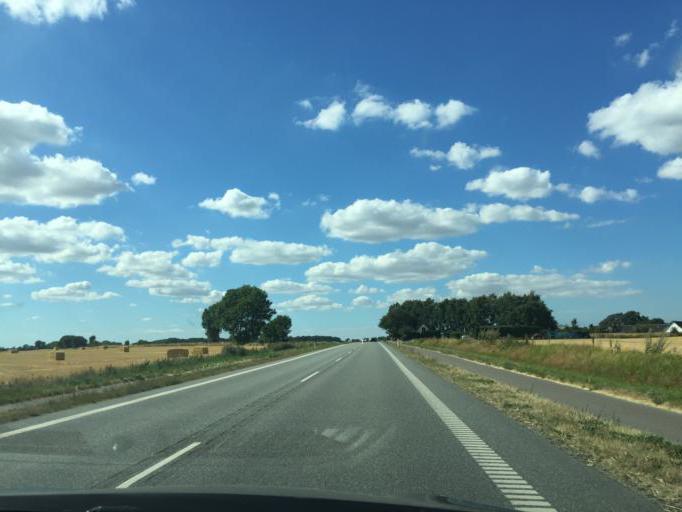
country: DK
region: South Denmark
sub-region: Odense Kommune
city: Hojby
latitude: 55.3341
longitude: 10.3897
